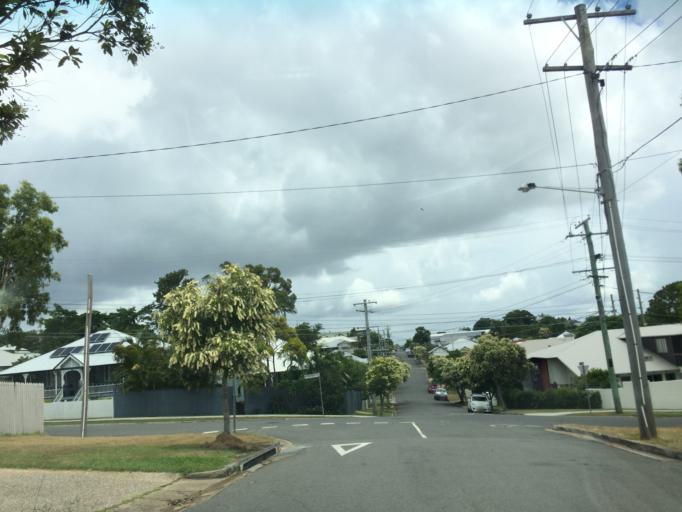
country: AU
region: Queensland
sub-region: Brisbane
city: Balmoral
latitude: -27.4466
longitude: 153.0588
